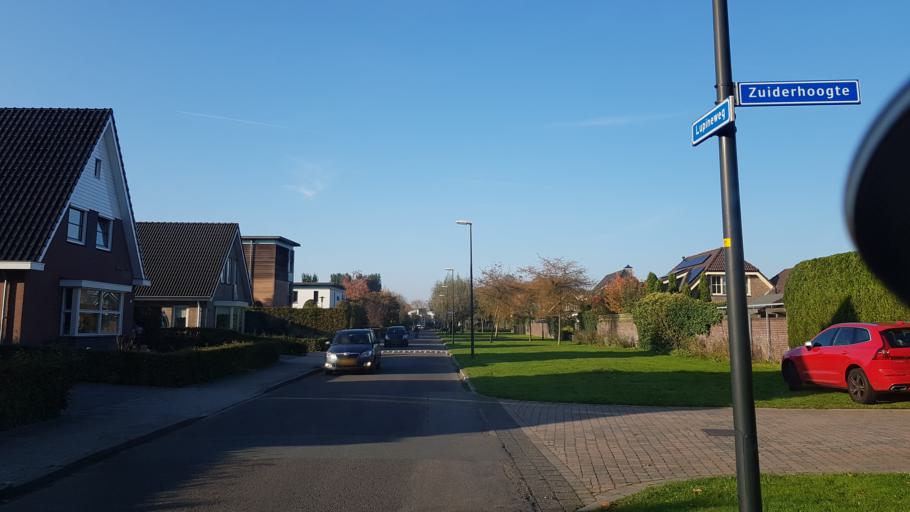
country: NL
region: Gelderland
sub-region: Gemeente Apeldoorn
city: Apeldoorn
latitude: 52.2149
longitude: 6.0182
